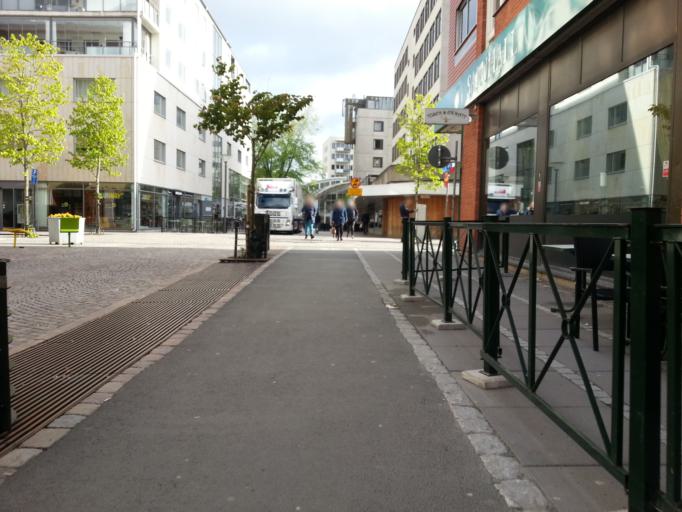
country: SE
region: Joenkoeping
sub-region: Jonkopings Kommun
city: Jonkoping
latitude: 57.7824
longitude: 14.1615
